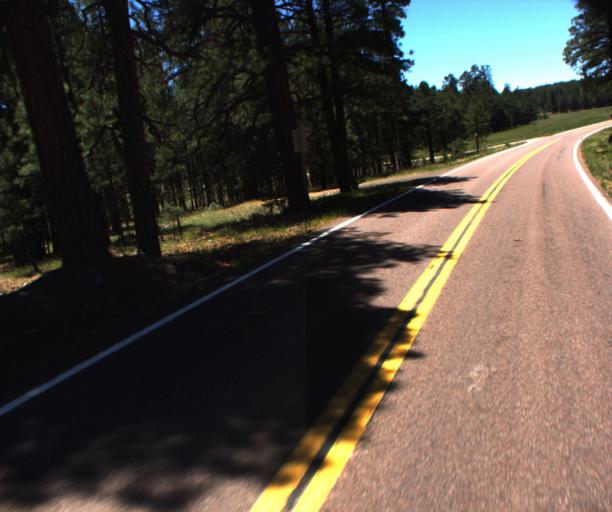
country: US
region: Arizona
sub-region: Gila County
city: Pine
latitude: 34.5392
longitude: -111.3289
